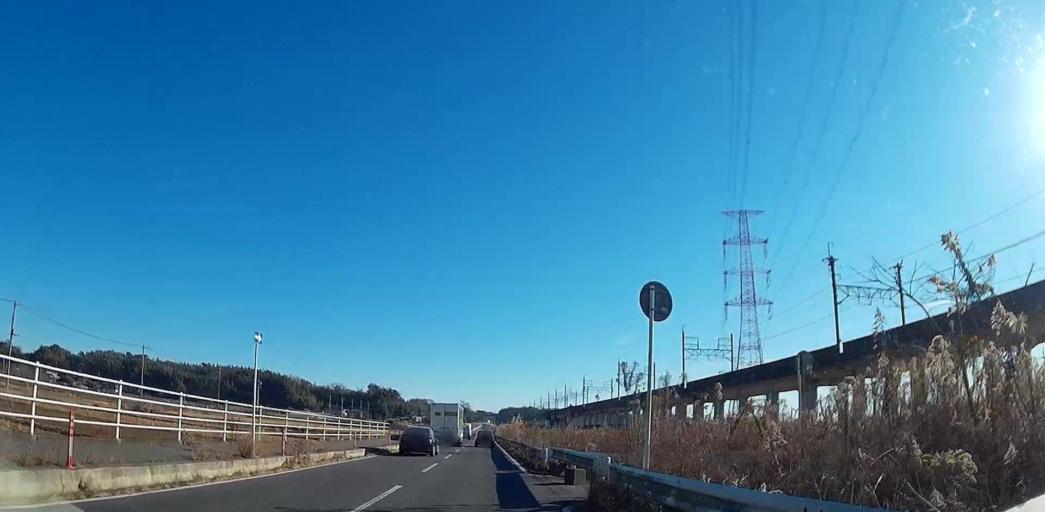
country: JP
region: Chiba
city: Shiroi
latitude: 35.7878
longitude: 140.0821
